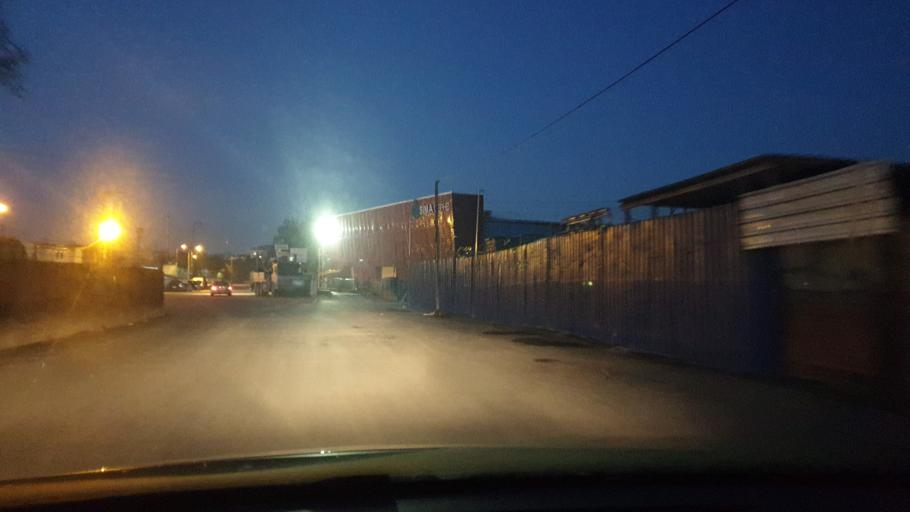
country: TR
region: Istanbul
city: Pendik
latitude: 40.9014
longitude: 29.2951
